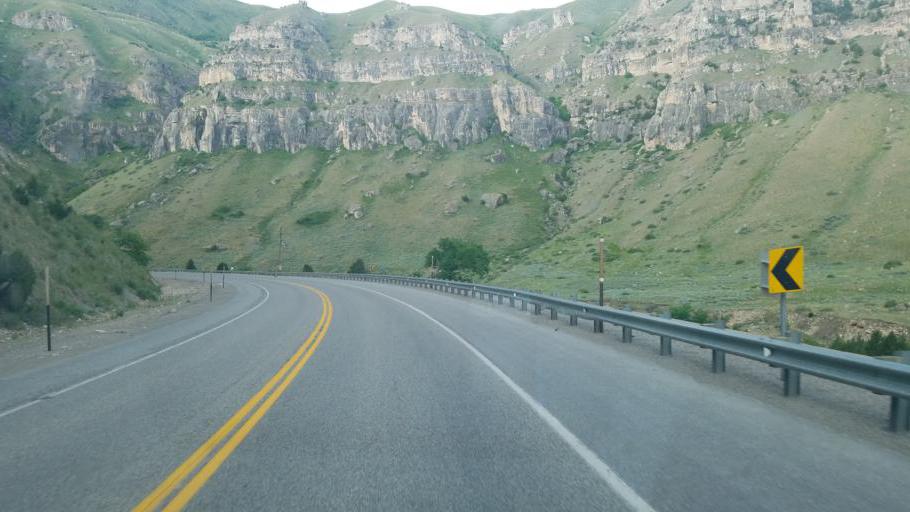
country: US
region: Wyoming
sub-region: Hot Springs County
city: Thermopolis
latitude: 43.5155
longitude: -108.1850
